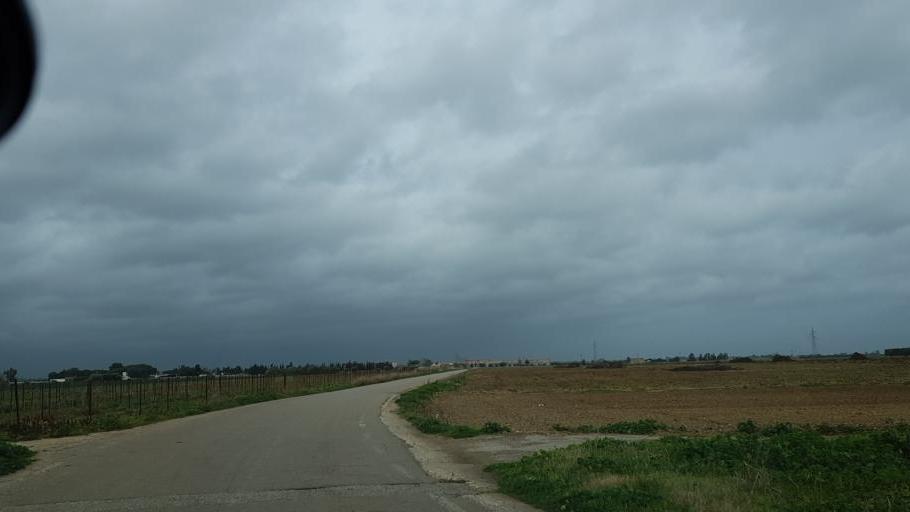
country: IT
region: Apulia
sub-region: Provincia di Brindisi
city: Brindisi
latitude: 40.6020
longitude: 17.8934
